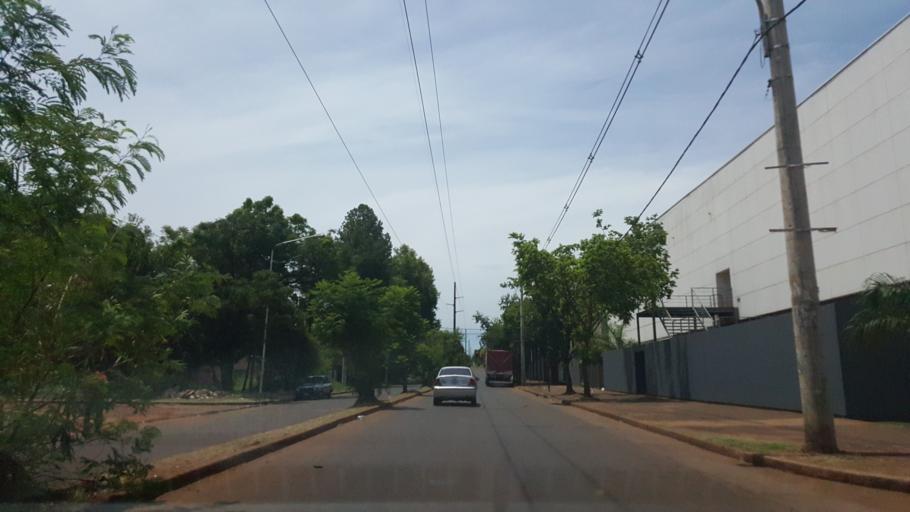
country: AR
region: Misiones
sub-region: Departamento de Capital
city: Posadas
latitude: -27.4019
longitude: -55.9175
